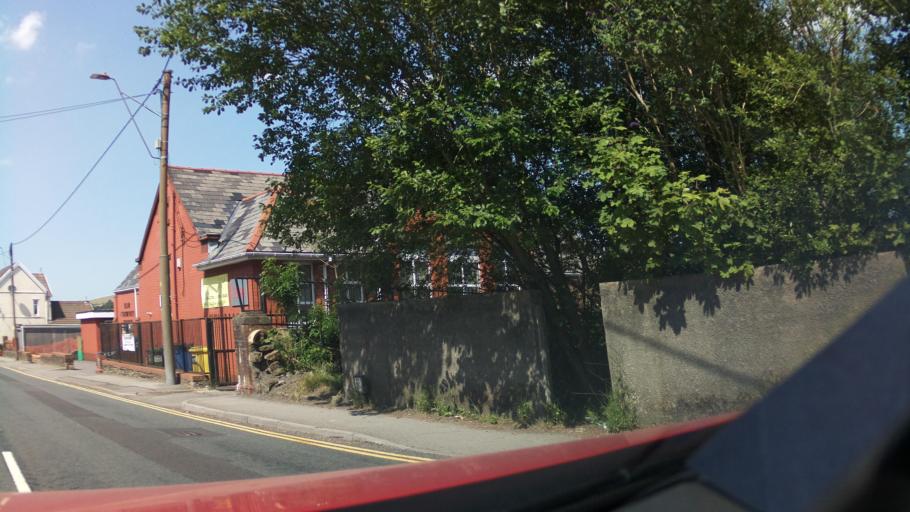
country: GB
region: Wales
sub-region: Caerphilly County Borough
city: Rhymney
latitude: 51.7438
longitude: -3.2787
